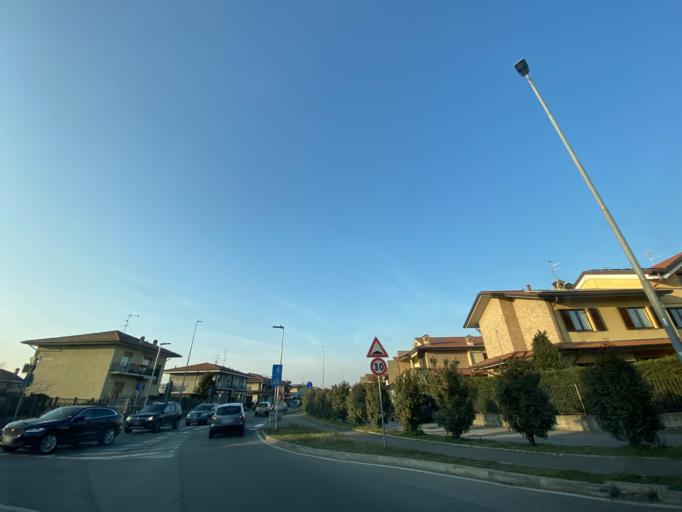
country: IT
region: Lombardy
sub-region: Citta metropolitana di Milano
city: Lainate
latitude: 45.5566
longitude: 9.0290
